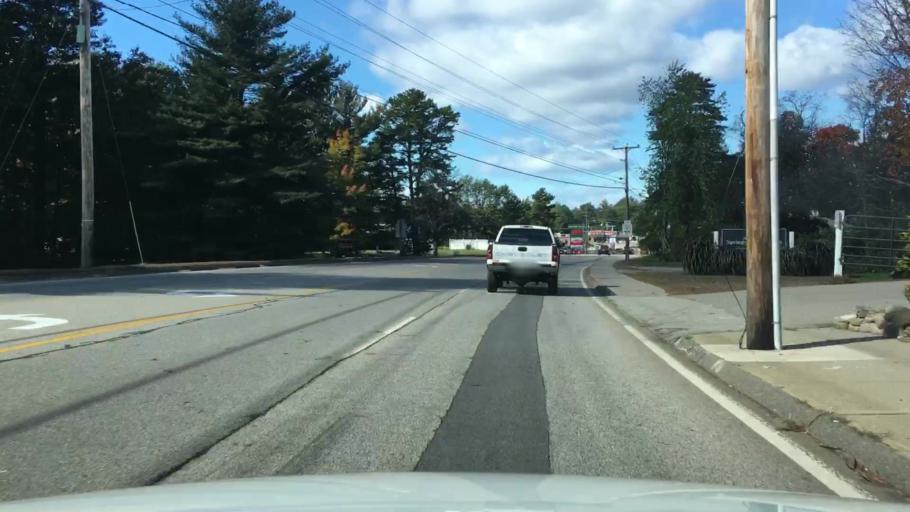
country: US
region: Maine
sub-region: York County
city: South Sanford
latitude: 43.4173
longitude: -70.7537
